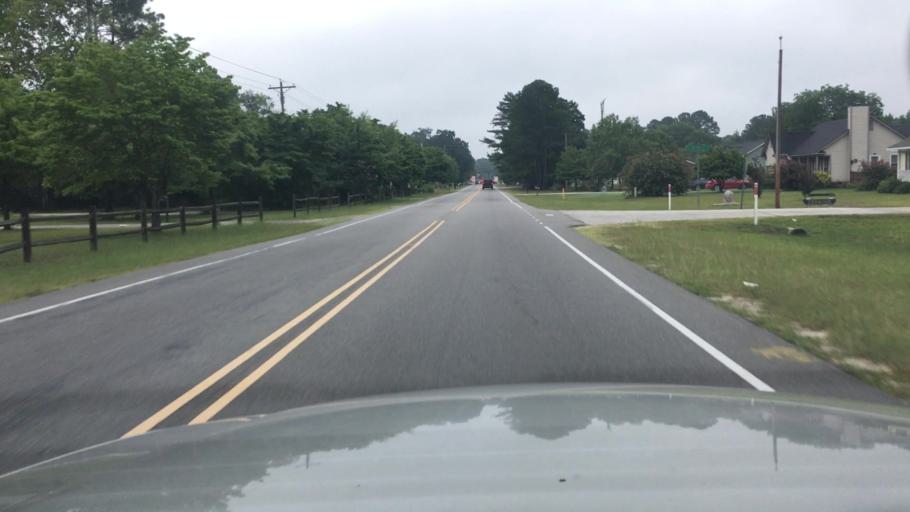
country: US
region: North Carolina
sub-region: Cumberland County
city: Hope Mills
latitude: 34.9758
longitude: -78.9931
